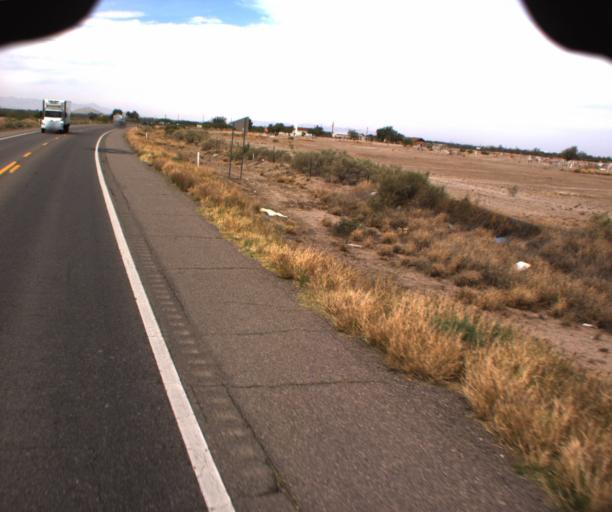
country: US
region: Arizona
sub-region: Pinal County
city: Sacaton
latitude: 33.1220
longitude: -111.7401
